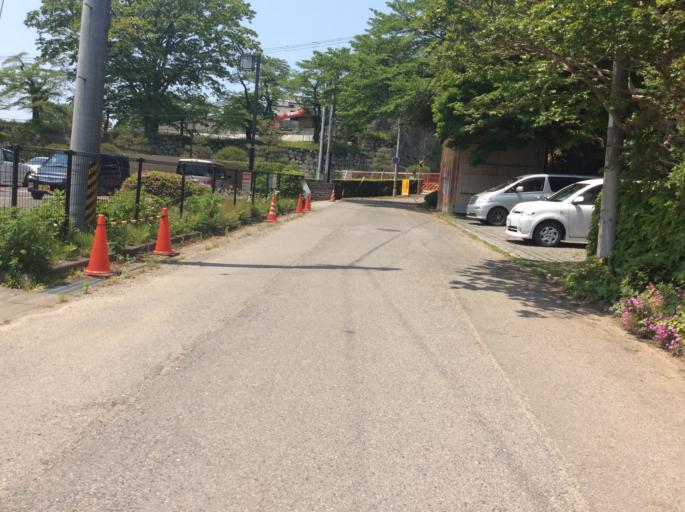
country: JP
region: Fukushima
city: Sukagawa
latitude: 37.1324
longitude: 140.2155
